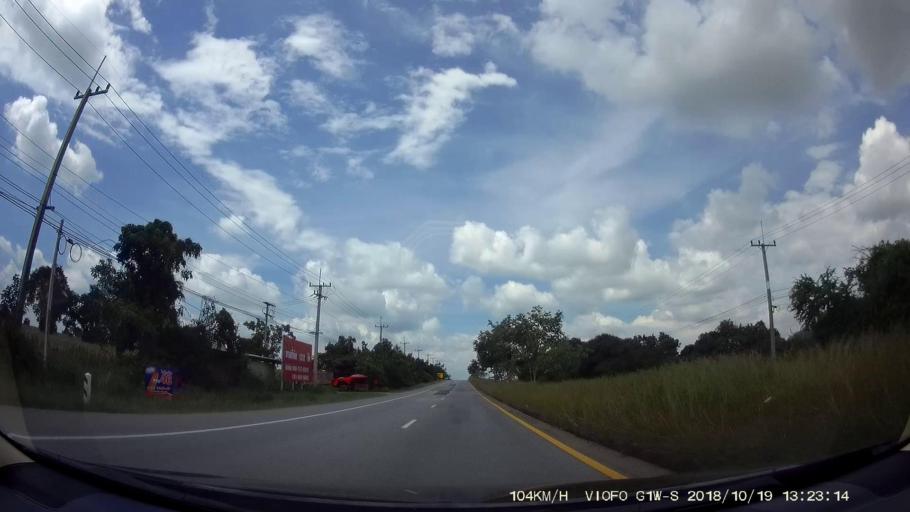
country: TH
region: Chaiyaphum
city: Chatturat
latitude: 15.4888
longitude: 101.8219
